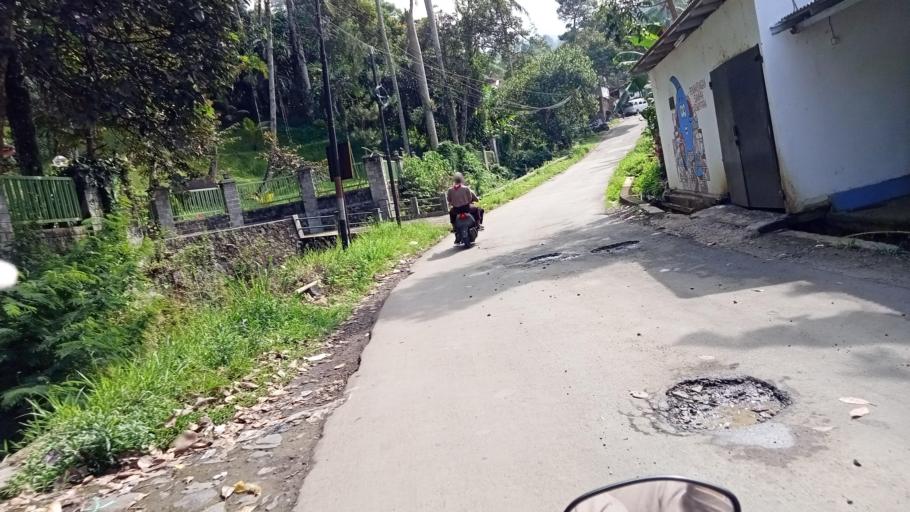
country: ID
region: West Java
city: Caringin
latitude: -6.6457
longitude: 106.9096
